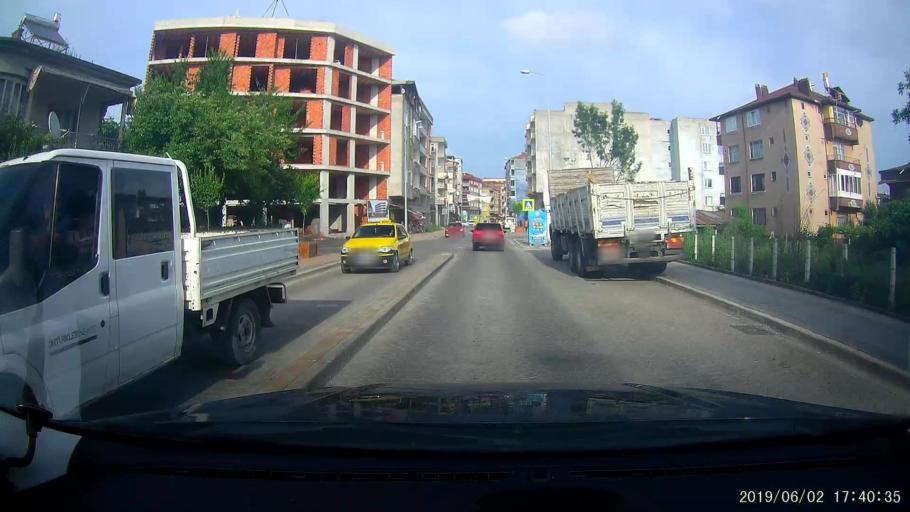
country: TR
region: Samsun
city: Terme
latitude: 41.2110
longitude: 36.9666
